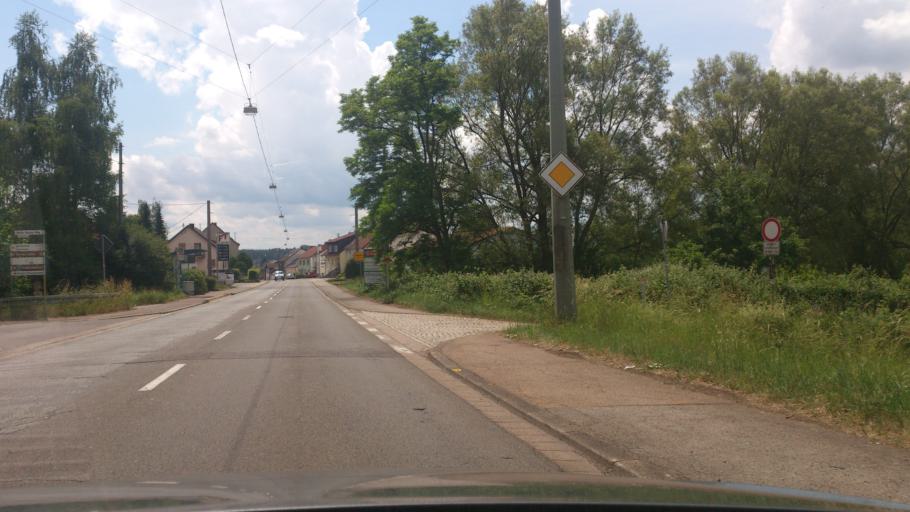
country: DE
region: Saarland
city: Schwalbach
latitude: 49.3133
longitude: 6.8215
